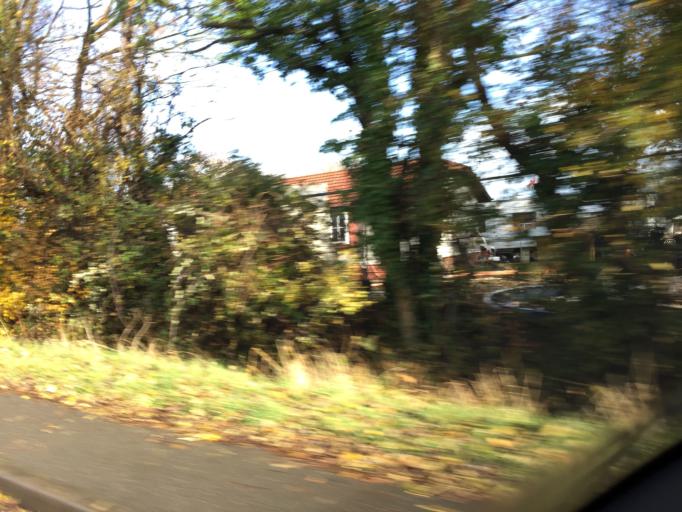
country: GB
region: England
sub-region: South Gloucestershire
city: Yate
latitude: 51.5616
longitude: -2.4374
